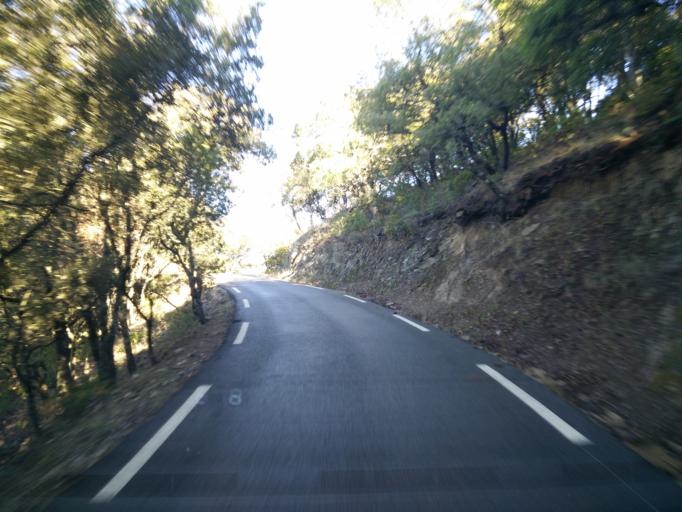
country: FR
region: Provence-Alpes-Cote d'Azur
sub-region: Departement du Var
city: Collobrieres
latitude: 43.2352
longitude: 6.3710
